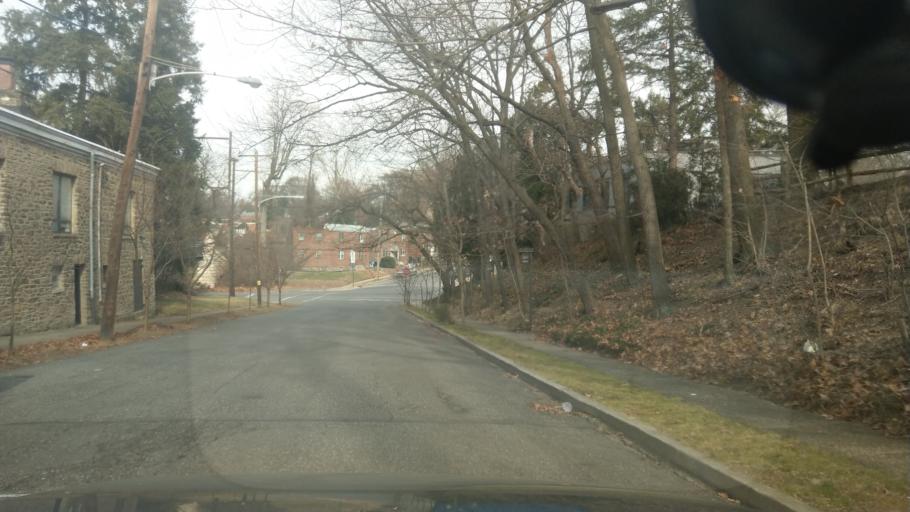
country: US
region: Pennsylvania
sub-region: Montgomery County
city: Wyncote
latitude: 40.0482
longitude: -75.1345
